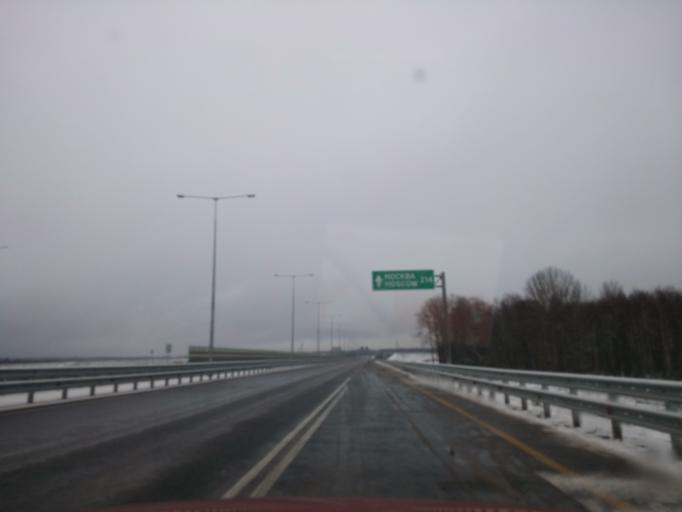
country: RU
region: Tverskaya
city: Likhoslavl'
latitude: 56.9807
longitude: 35.4255
